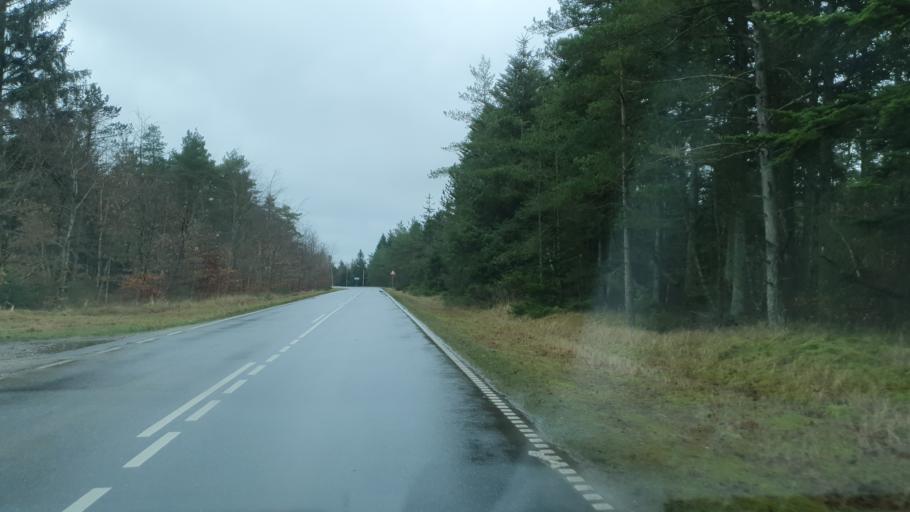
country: DK
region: North Denmark
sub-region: Jammerbugt Kommune
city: Fjerritslev
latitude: 57.1283
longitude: 9.1322
